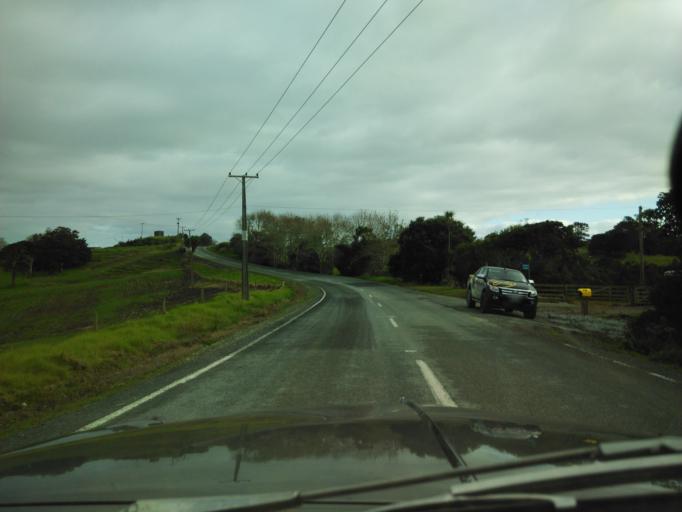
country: NZ
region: Auckland
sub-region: Auckland
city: Wellsford
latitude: -36.3295
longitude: 174.4148
